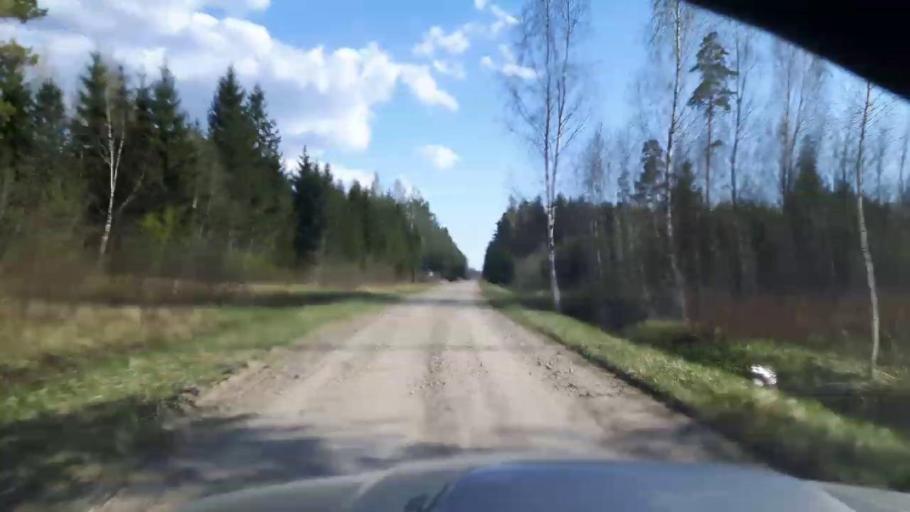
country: EE
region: Paernumaa
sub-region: Tootsi vald
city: Tootsi
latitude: 58.4264
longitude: 24.8515
